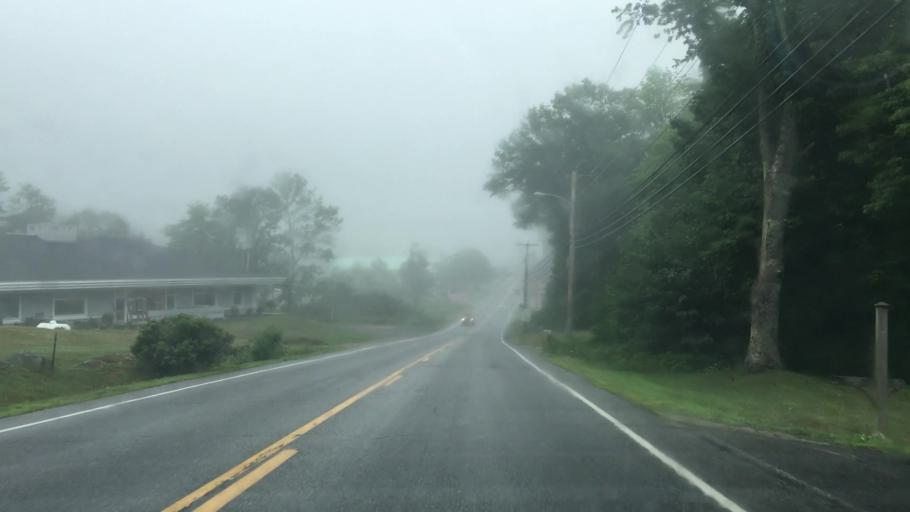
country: US
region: Maine
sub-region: Lincoln County
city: Boothbay
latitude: 43.8686
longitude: -69.6303
